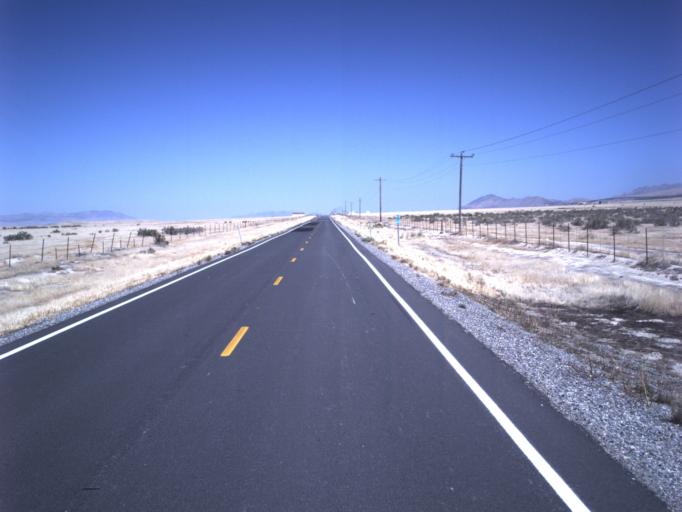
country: US
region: Utah
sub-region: Tooele County
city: Grantsville
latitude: 40.3692
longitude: -112.7463
